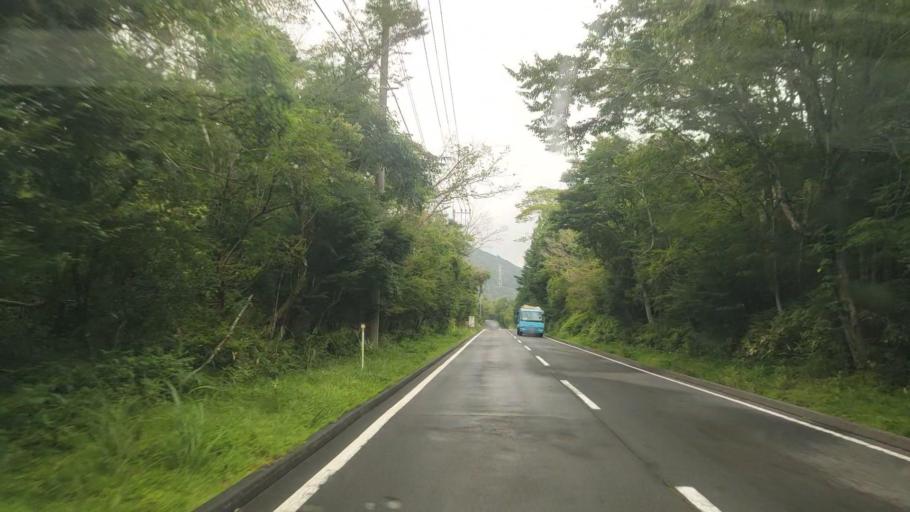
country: JP
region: Shizuoka
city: Gotemba
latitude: 35.2774
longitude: 138.7953
